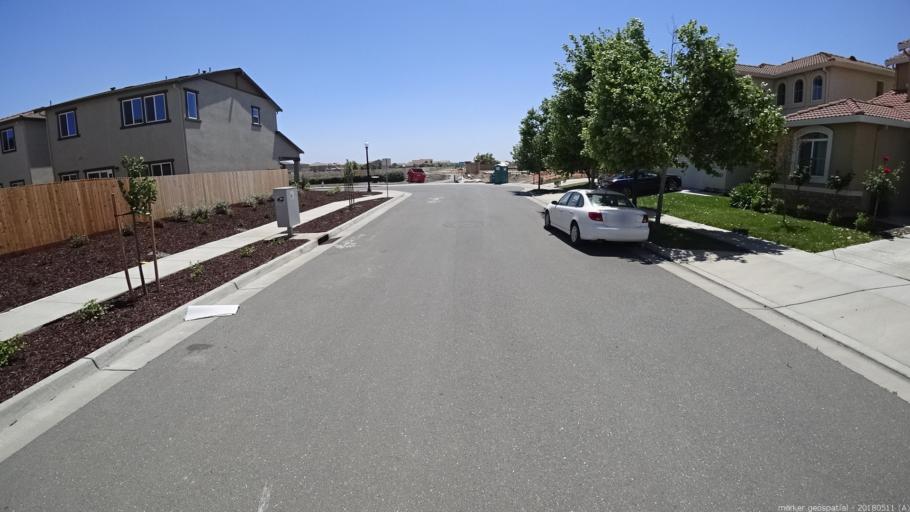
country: US
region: California
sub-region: Yolo County
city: West Sacramento
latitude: 38.6502
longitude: -121.5476
